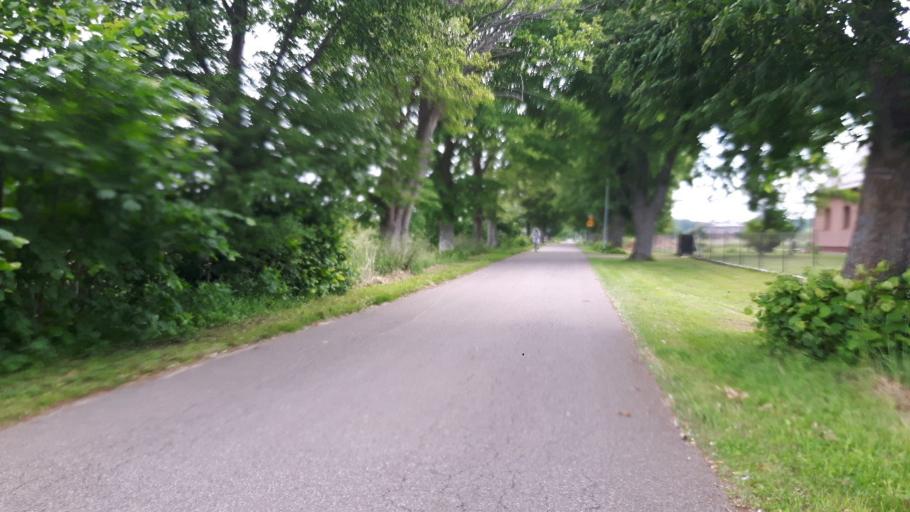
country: PL
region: Pomeranian Voivodeship
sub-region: Powiat leborski
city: Leba
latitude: 54.7522
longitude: 17.6015
